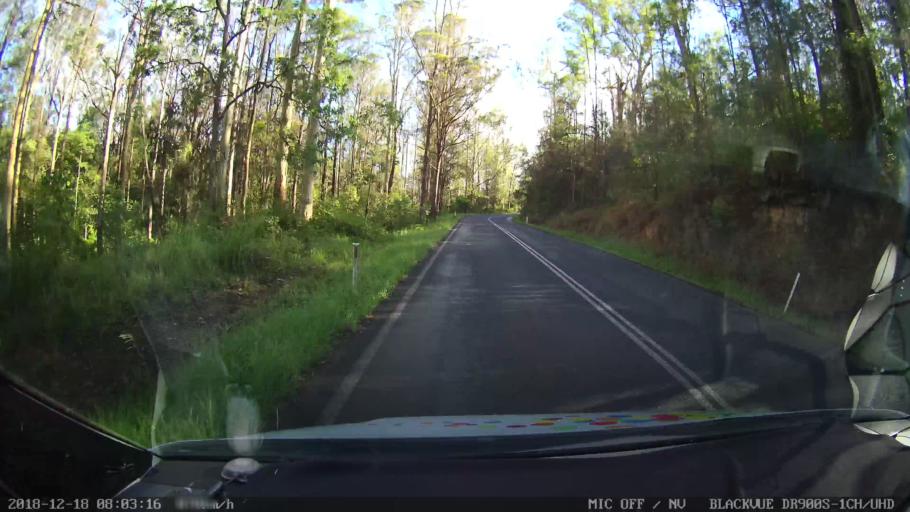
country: AU
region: New South Wales
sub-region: Kyogle
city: Kyogle
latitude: -28.3867
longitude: 152.6393
